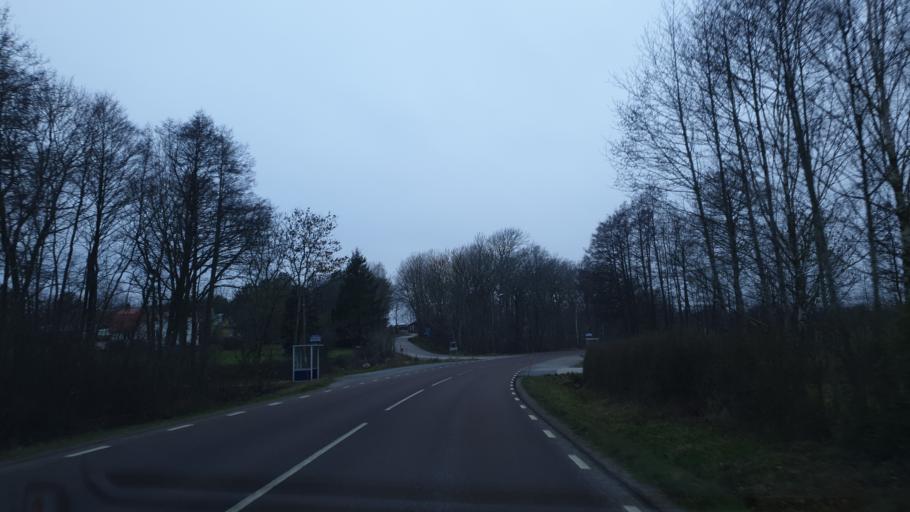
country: SE
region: Blekinge
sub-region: Karlskrona Kommun
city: Jaemjoe
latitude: 56.1675
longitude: 15.7480
